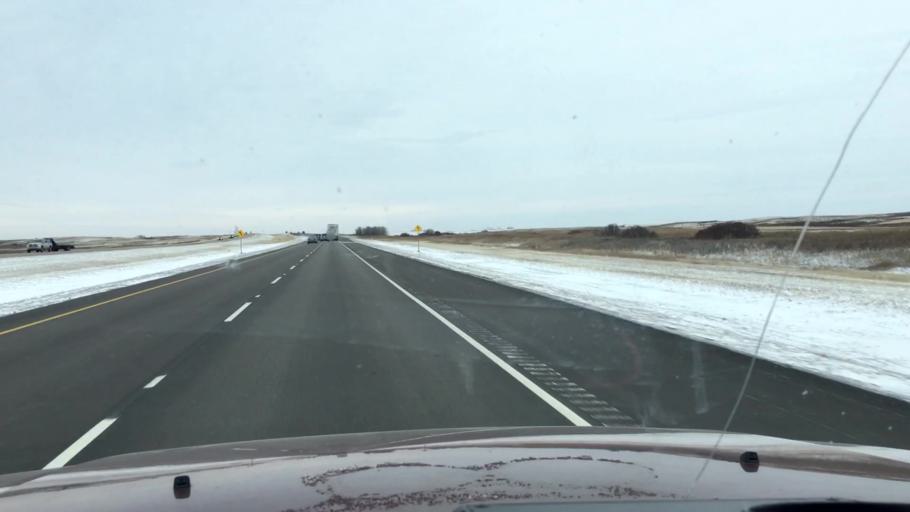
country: CA
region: Saskatchewan
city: Moose Jaw
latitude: 50.8877
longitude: -105.6237
